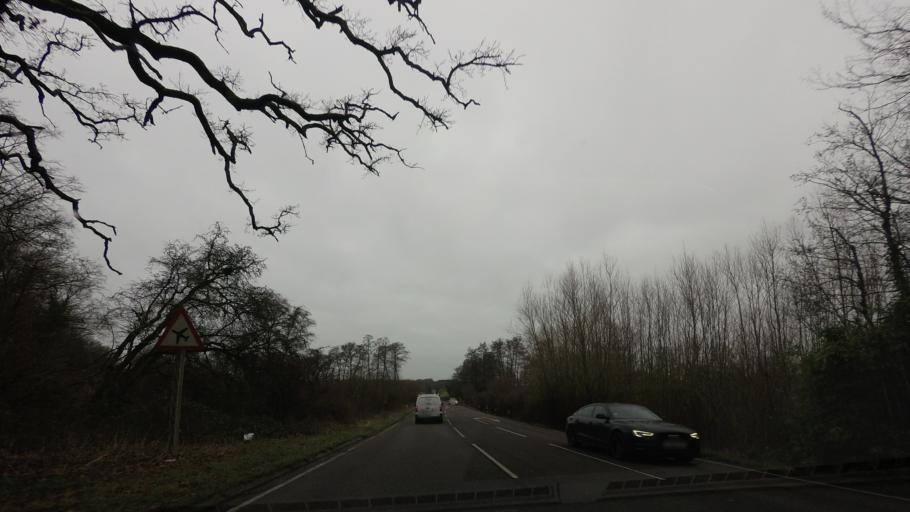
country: GB
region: England
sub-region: East Sussex
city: Battle
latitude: 50.9303
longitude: 0.5254
